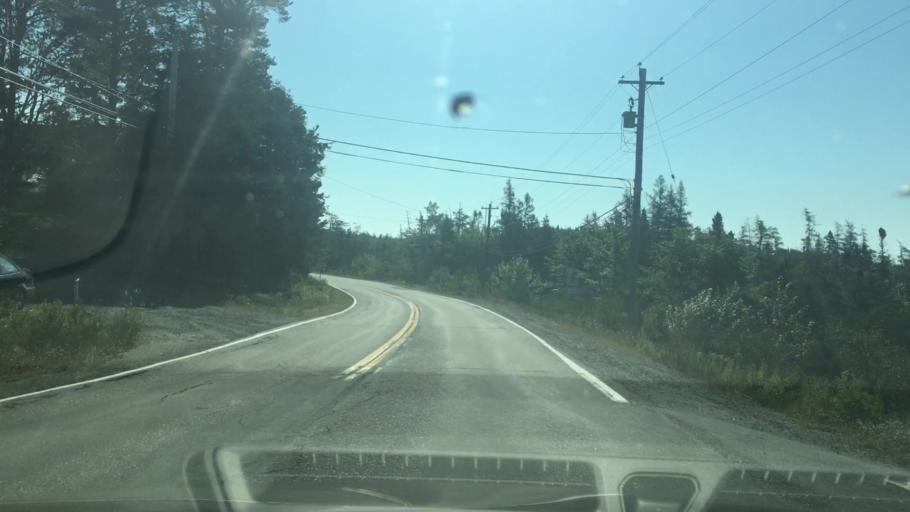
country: CA
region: Nova Scotia
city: Cole Harbour
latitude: 44.7757
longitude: -63.0552
